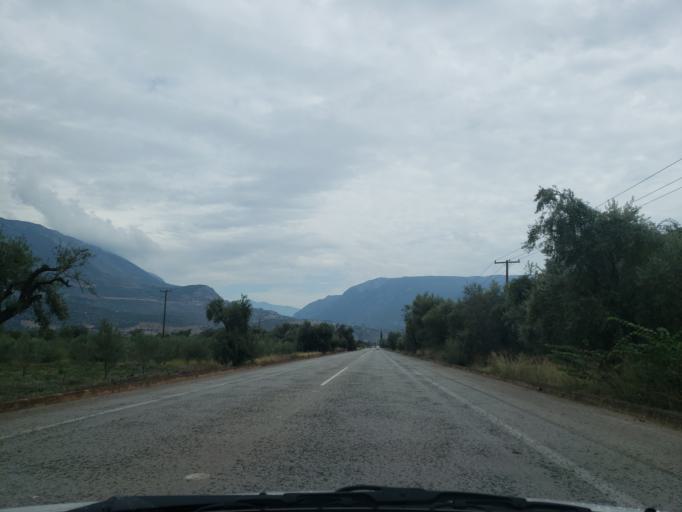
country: GR
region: Central Greece
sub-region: Nomos Fokidos
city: Itea
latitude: 38.4832
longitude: 22.4264
